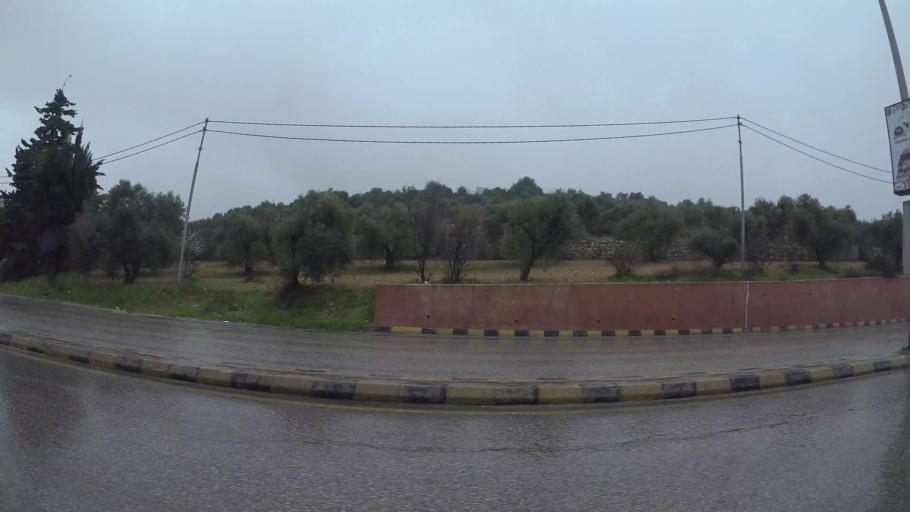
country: JO
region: Amman
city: Wadi as Sir
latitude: 32.0017
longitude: 35.8010
